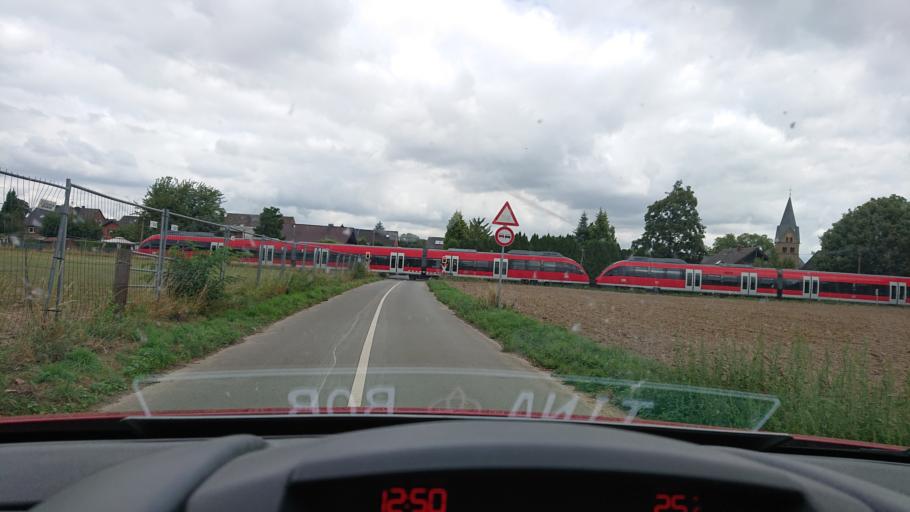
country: DE
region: North Rhine-Westphalia
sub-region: Regierungsbezirk Koln
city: Bergheim
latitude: 50.9620
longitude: 6.6049
